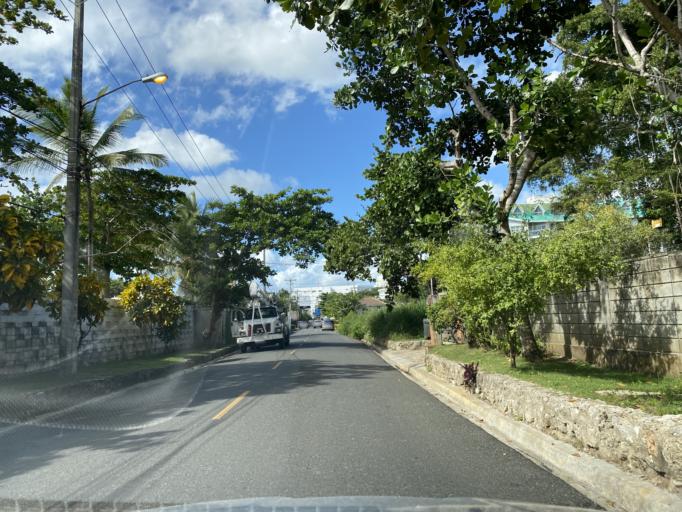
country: DO
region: Santo Domingo
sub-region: Santo Domingo
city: Boca Chica
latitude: 18.4485
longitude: -69.6004
